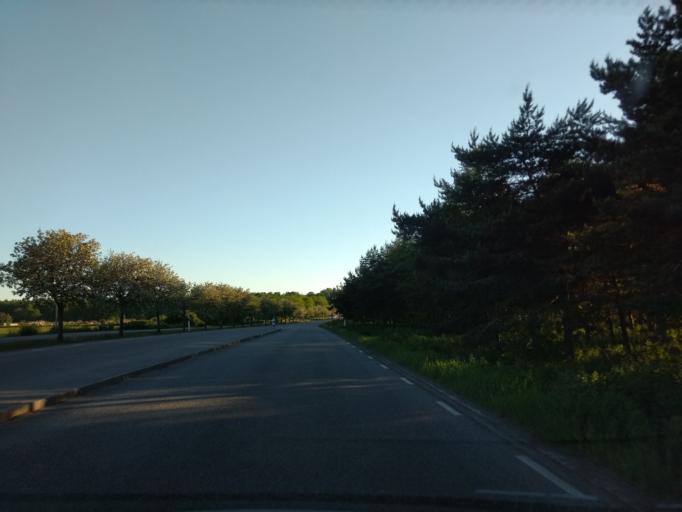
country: SE
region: Uppsala
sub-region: Uppsala Kommun
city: Uppsala
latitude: 59.8438
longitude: 17.6635
